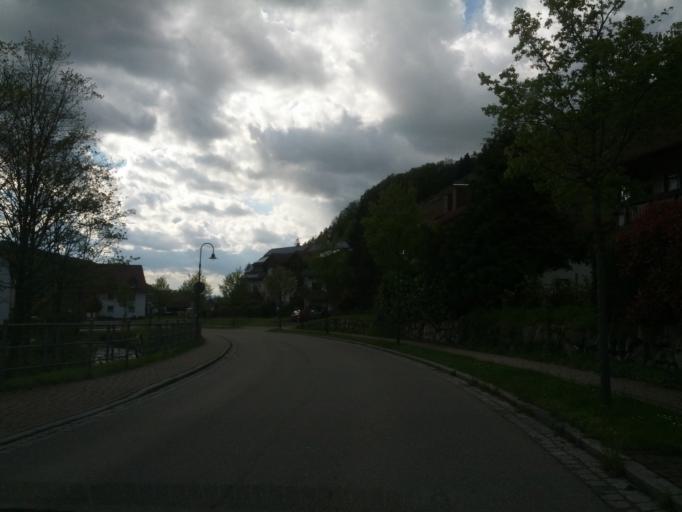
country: DE
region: Baden-Wuerttemberg
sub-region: Freiburg Region
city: Glottertal
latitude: 48.0486
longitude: 7.9535
